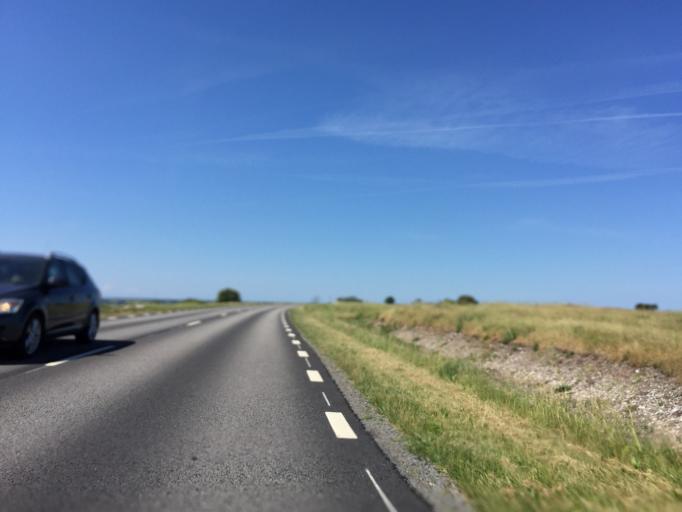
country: SE
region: Skane
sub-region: Trelleborgs Kommun
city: Skare
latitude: 55.3826
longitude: 13.0278
